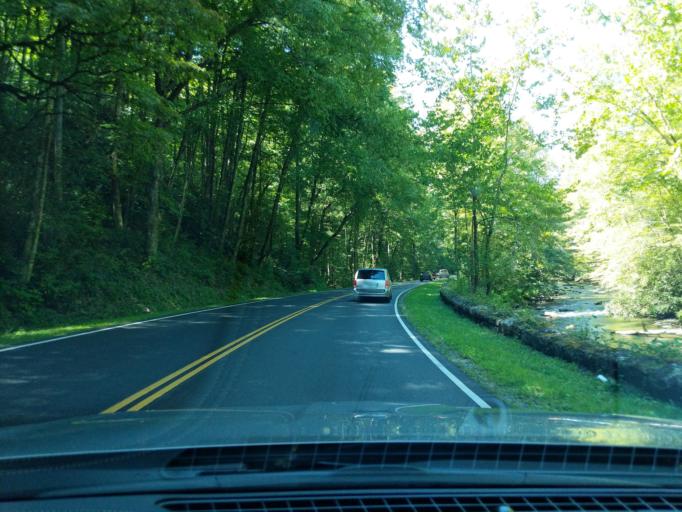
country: US
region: North Carolina
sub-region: Swain County
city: Cherokee
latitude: 35.5438
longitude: -83.3025
